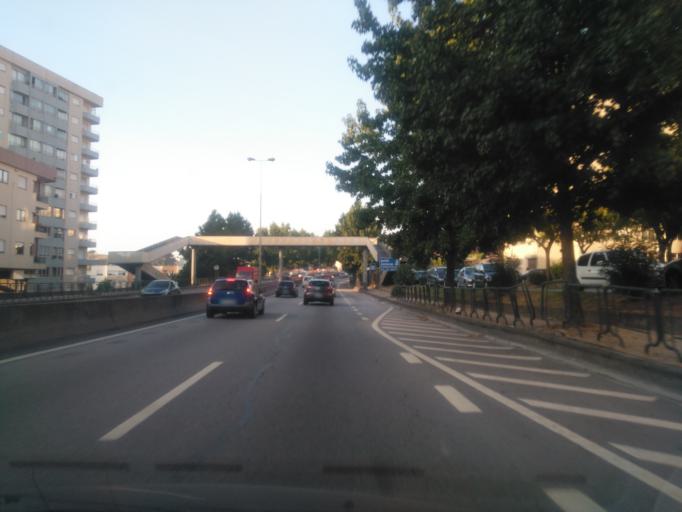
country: PT
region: Braga
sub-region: Braga
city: Braga
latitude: 41.5554
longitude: -8.4291
